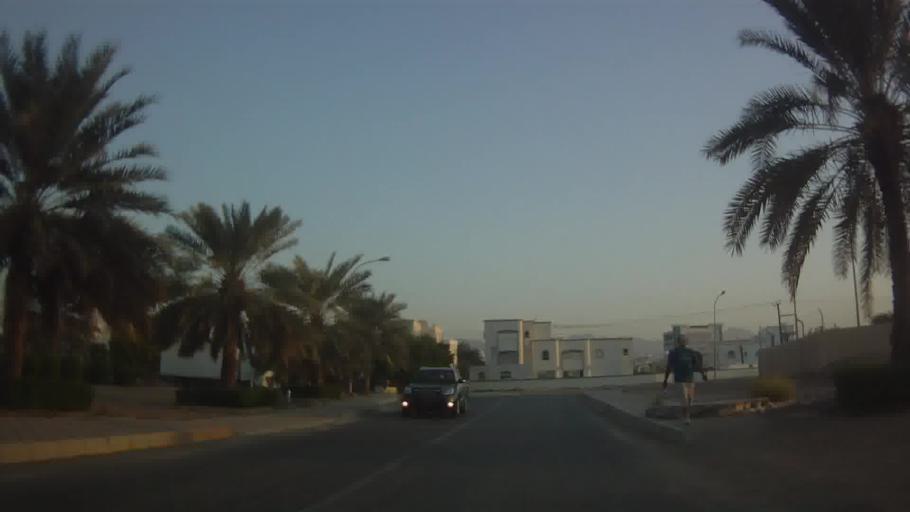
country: OM
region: Muhafazat Masqat
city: Bawshar
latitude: 23.5990
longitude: 58.4032
